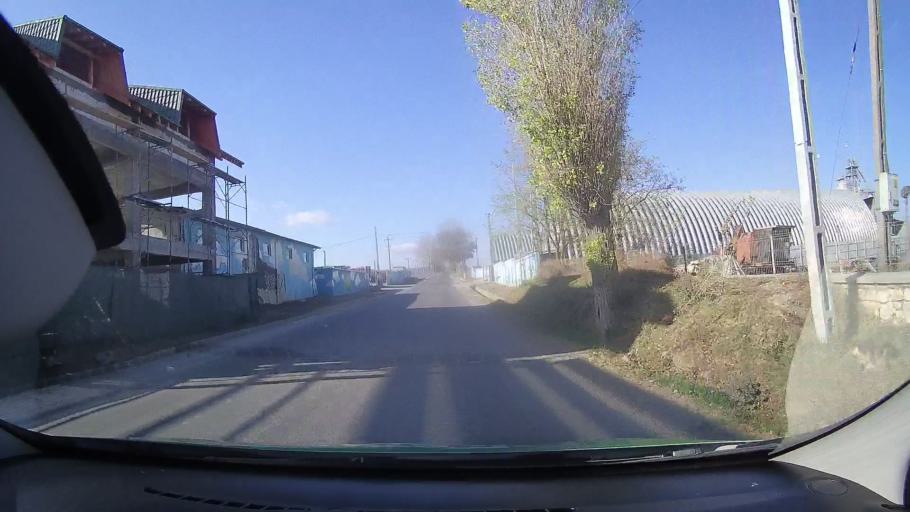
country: RO
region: Tulcea
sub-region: Comuna Sarichioi
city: Enisala
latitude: 44.8786
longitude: 28.8042
